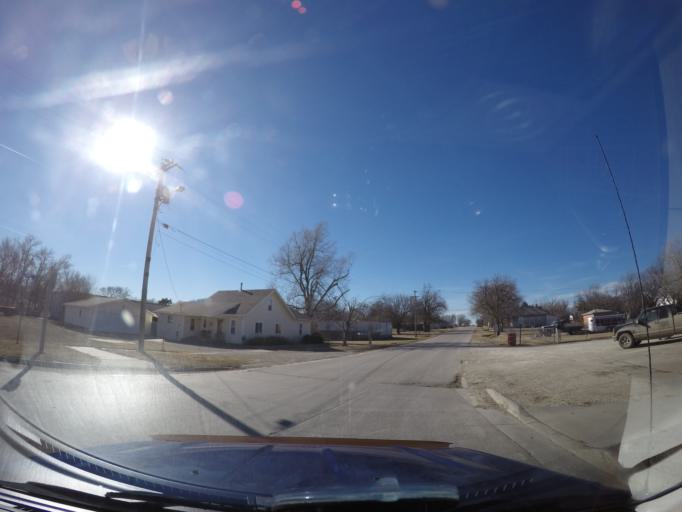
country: US
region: Kansas
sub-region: Marion County
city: Marion
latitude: 38.4935
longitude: -96.9580
